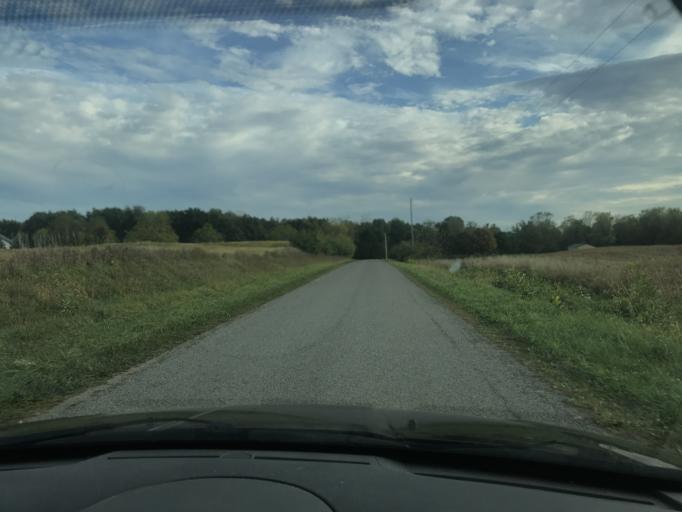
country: US
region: Ohio
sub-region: Logan County
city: West Liberty
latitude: 40.2825
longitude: -83.6851
